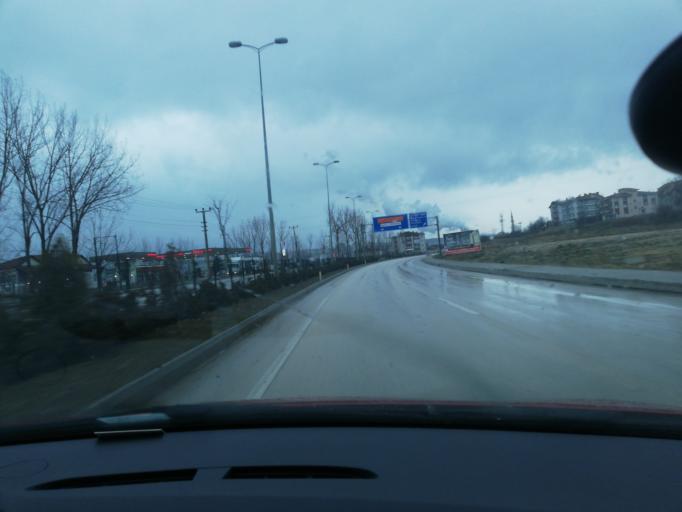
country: TR
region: Kastamonu
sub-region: Cide
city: Kastamonu
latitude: 41.4223
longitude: 33.8022
